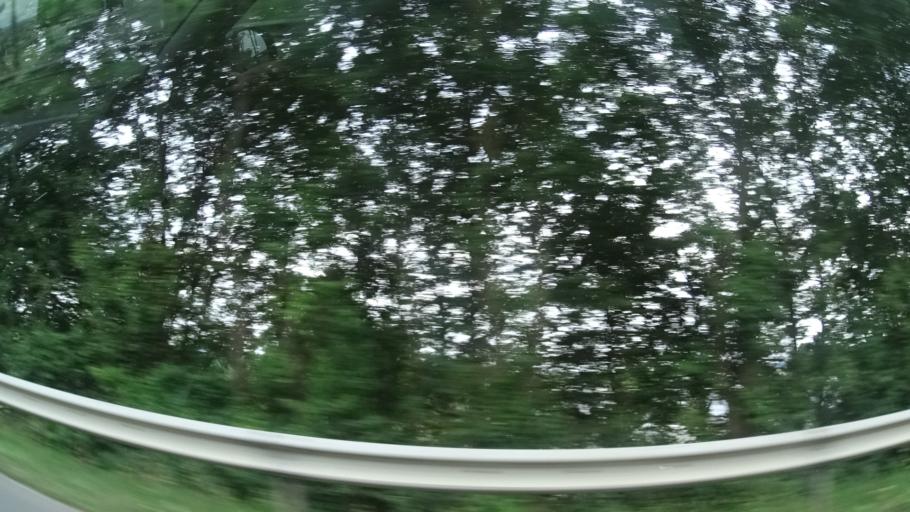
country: DE
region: North Rhine-Westphalia
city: Brakel
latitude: 51.7136
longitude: 9.1679
